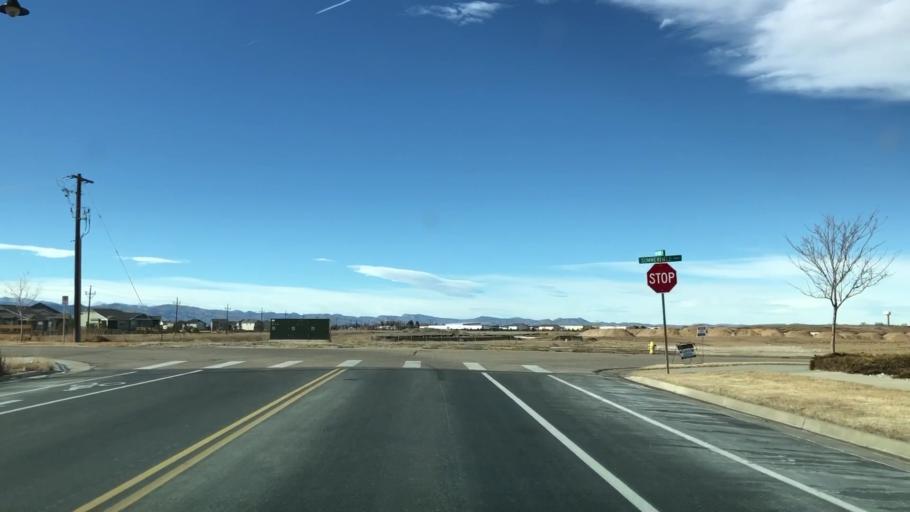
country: US
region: Colorado
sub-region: Weld County
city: Windsor
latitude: 40.5113
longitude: -104.9527
